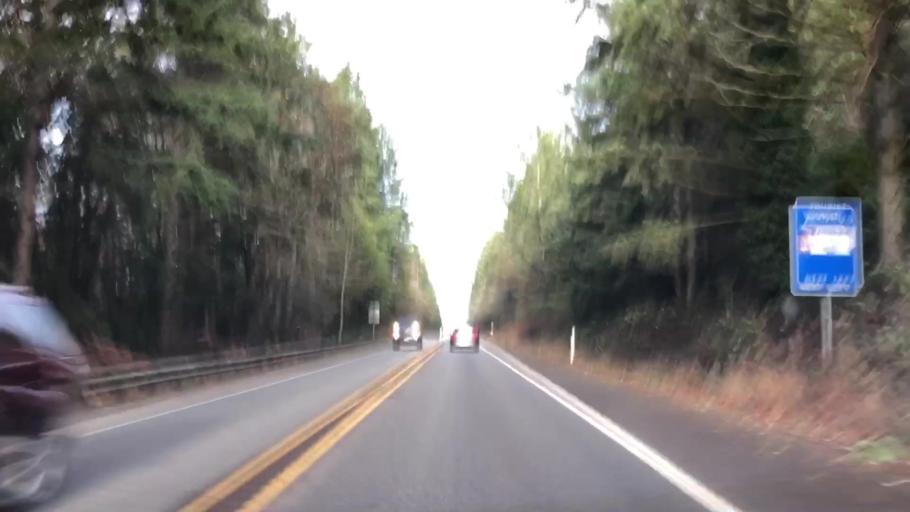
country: US
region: Washington
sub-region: Kitsap County
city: Bainbridge Island
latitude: 47.6748
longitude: -122.5343
